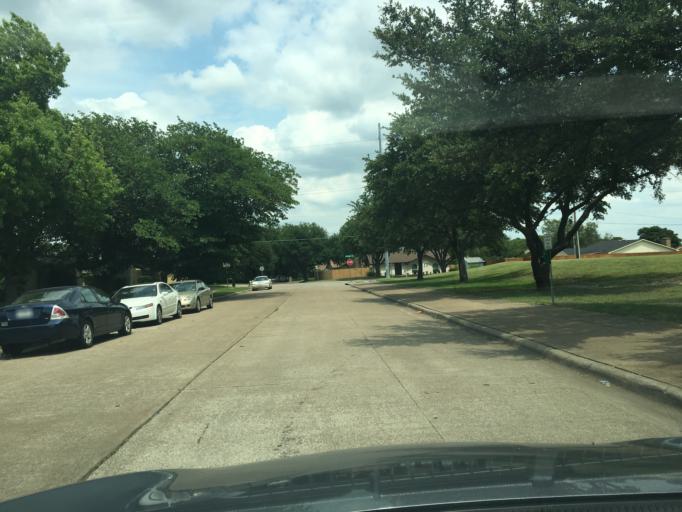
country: US
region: Texas
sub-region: Dallas County
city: Richardson
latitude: 32.9576
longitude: -96.6748
